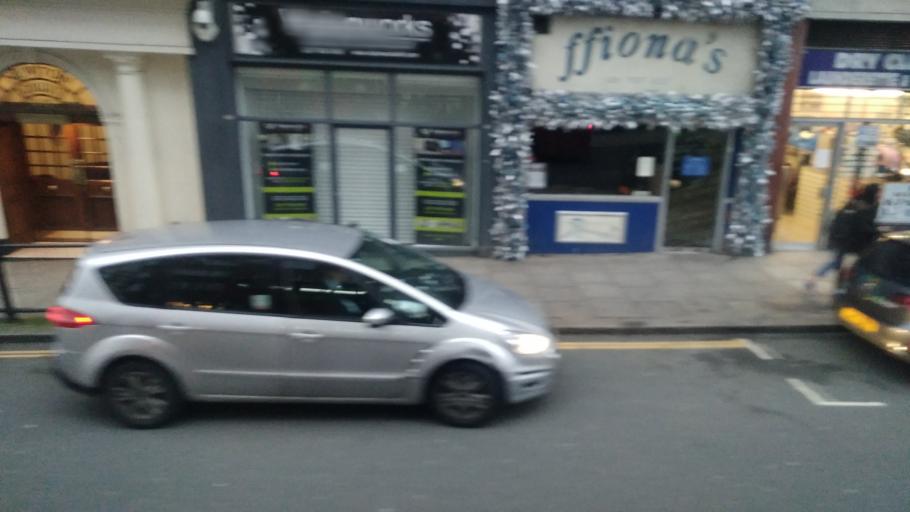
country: GB
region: England
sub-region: Greater London
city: Kensington
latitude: 51.5041
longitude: -0.1927
